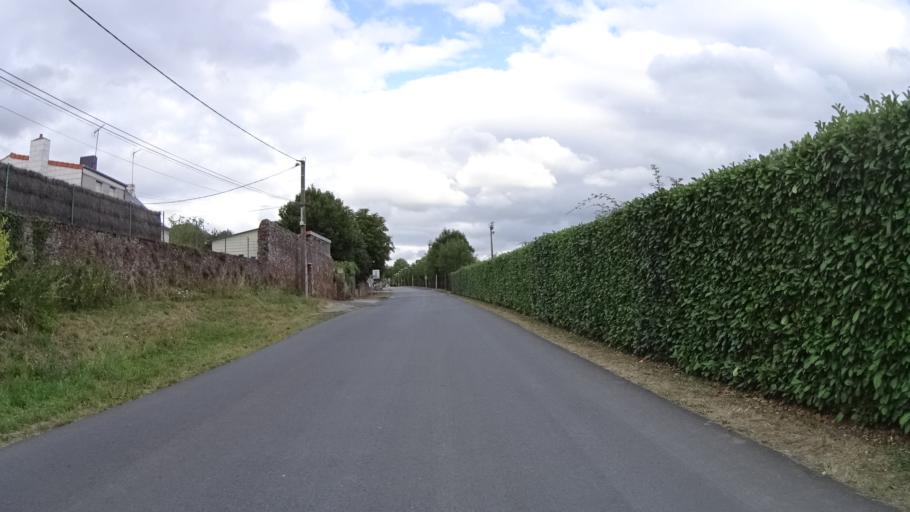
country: FR
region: Pays de la Loire
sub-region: Departement de la Loire-Atlantique
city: Saint-Gereon
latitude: 47.3634
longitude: -1.1915
